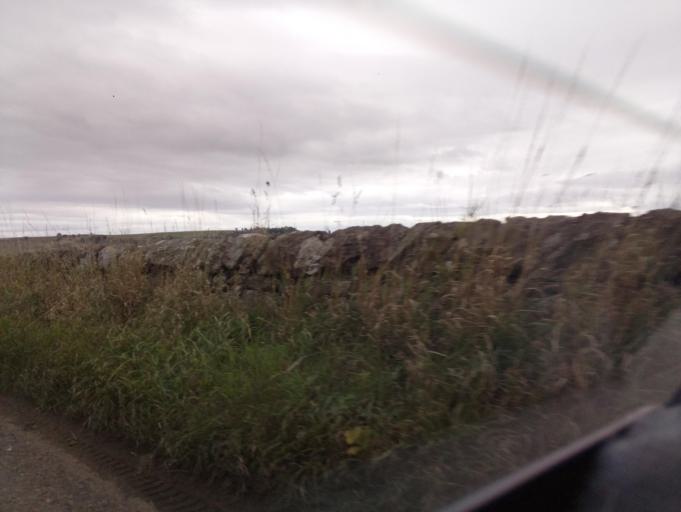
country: GB
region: Scotland
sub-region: Fife
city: Ballingry
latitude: 56.1995
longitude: -3.3023
